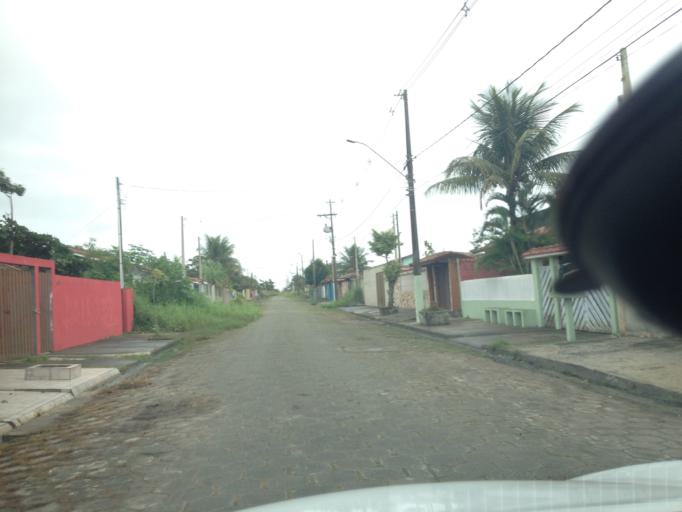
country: BR
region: Sao Paulo
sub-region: Itanhaem
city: Itanhaem
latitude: -24.2265
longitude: -46.8705
